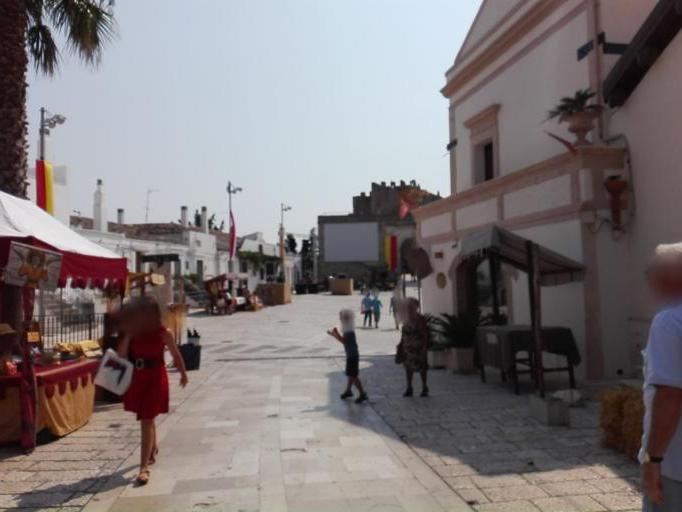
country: IT
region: Basilicate
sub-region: Provincia di Matera
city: Miglionico
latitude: 40.5685
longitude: 16.5006
